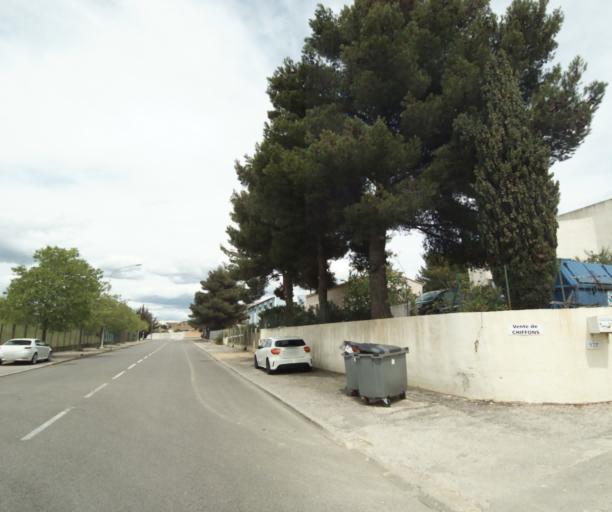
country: FR
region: Provence-Alpes-Cote d'Azur
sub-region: Departement des Bouches-du-Rhone
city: Rognac
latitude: 43.4797
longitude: 5.2347
